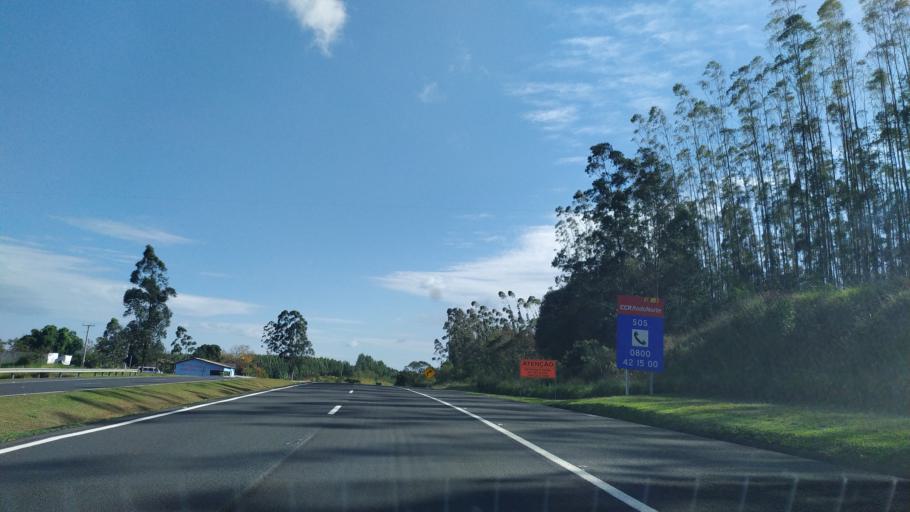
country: BR
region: Parana
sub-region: Telemaco Borba
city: Telemaco Borba
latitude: -24.4267
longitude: -50.7672
